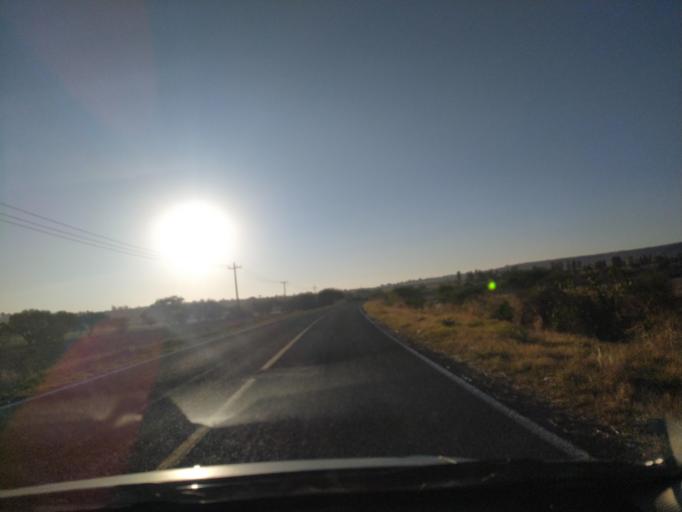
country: MX
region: Guanajuato
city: Ciudad Manuel Doblado
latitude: 20.7344
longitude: -101.8348
